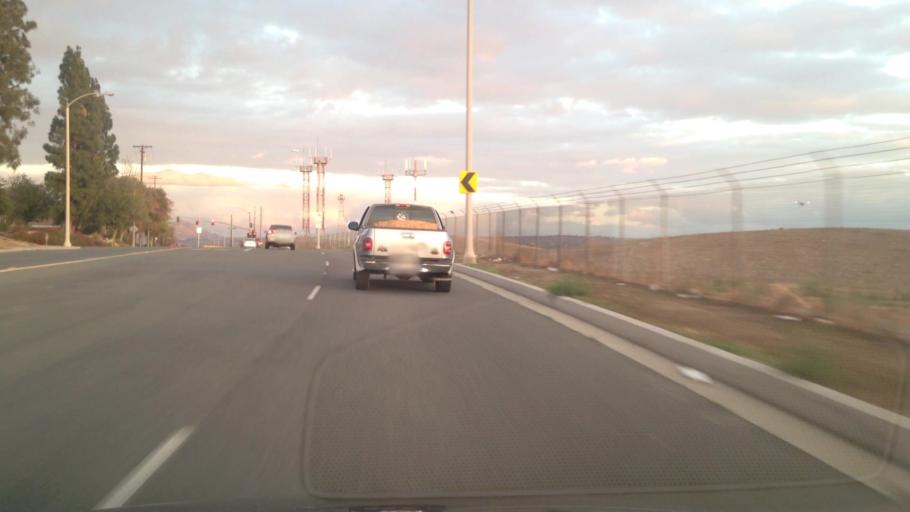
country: US
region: California
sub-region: Riverside County
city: Riverside
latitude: 33.9532
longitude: -117.4381
